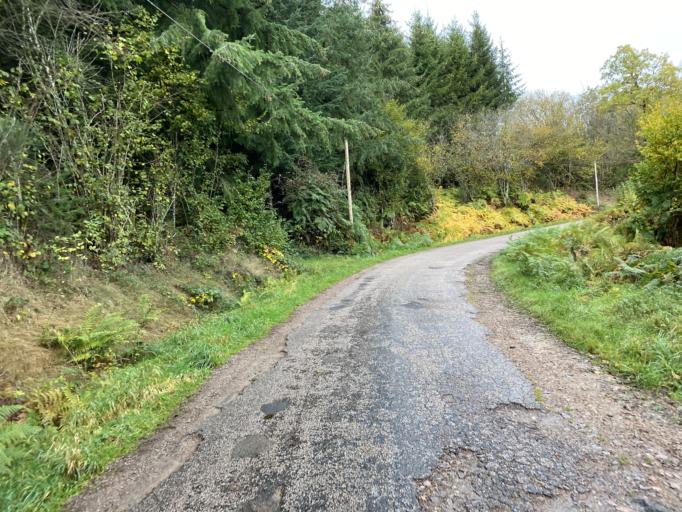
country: FR
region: Bourgogne
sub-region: Departement de la Cote-d'Or
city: Saulieu
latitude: 47.2619
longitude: 4.1717
